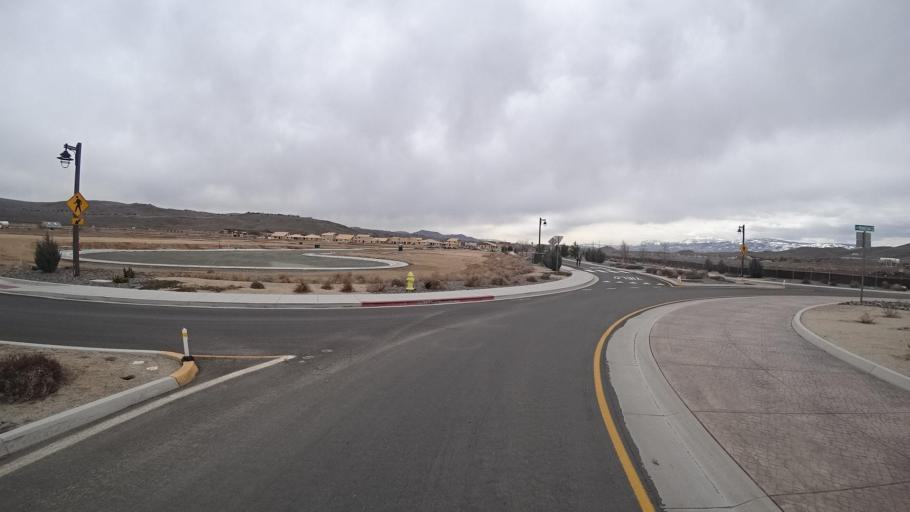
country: US
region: Nevada
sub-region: Washoe County
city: Spanish Springs
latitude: 39.6085
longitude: -119.7198
